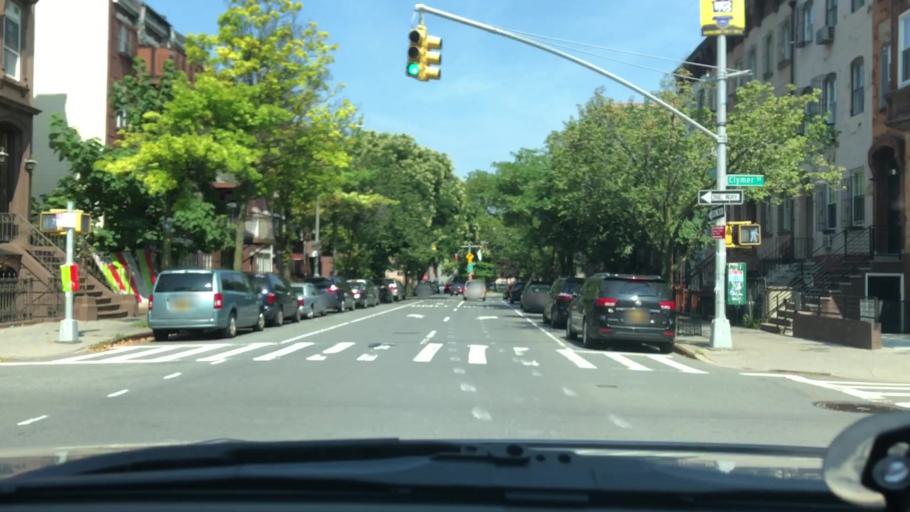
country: US
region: New York
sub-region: Queens County
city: Long Island City
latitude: 40.7064
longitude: -73.9637
